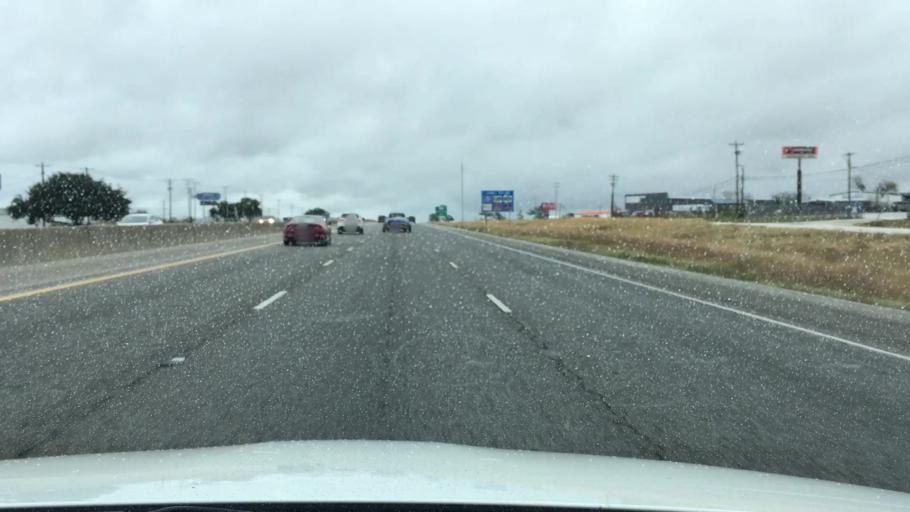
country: US
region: Texas
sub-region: Hays County
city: Buda
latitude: 30.0447
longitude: -97.8409
